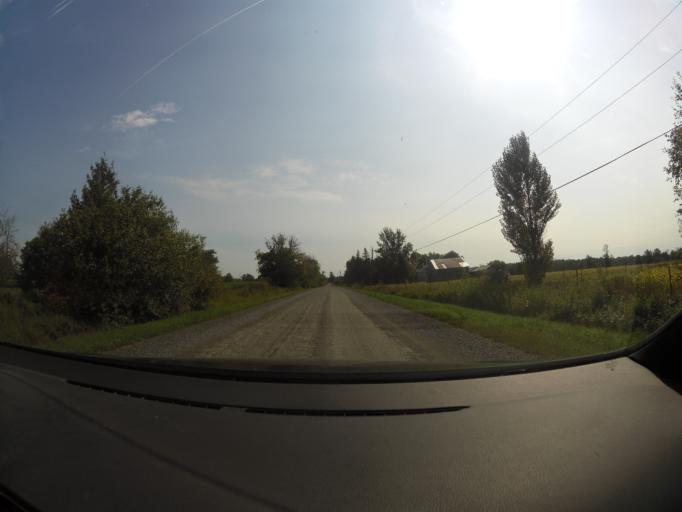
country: CA
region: Ontario
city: Arnprior
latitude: 45.3326
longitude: -76.1836
